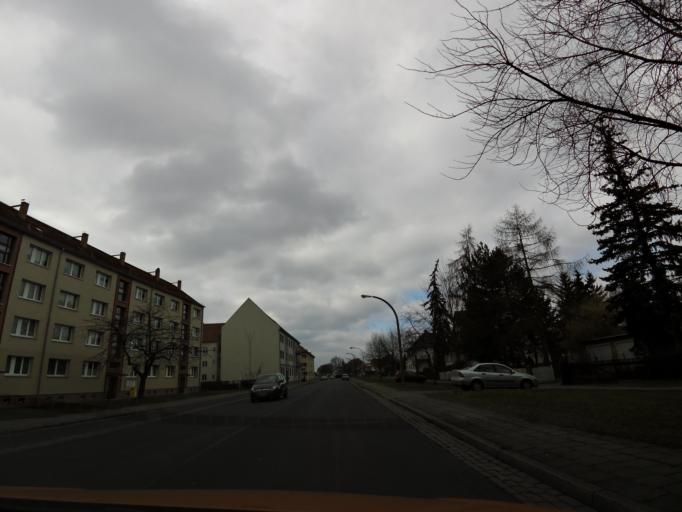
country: DE
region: Brandenburg
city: Rathenow
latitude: 52.6126
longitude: 12.3468
